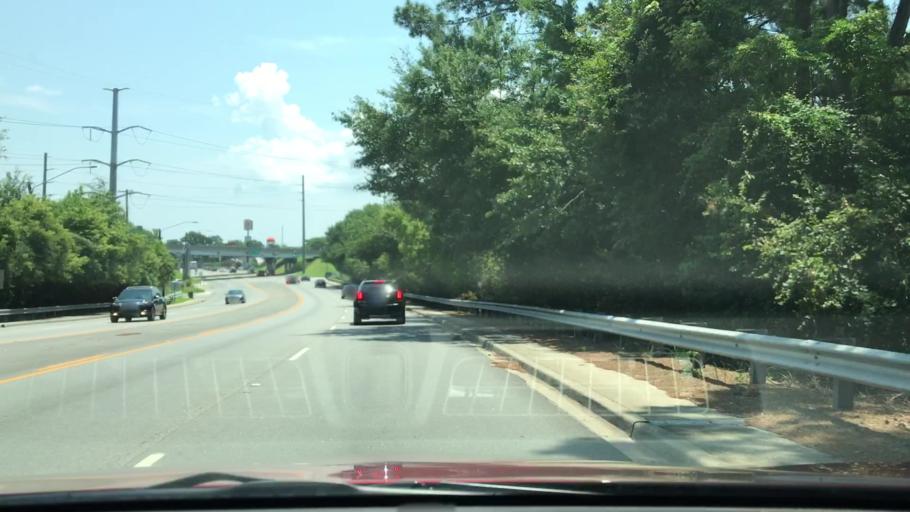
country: US
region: South Carolina
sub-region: Charleston County
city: North Charleston
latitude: 32.8553
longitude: -80.0240
